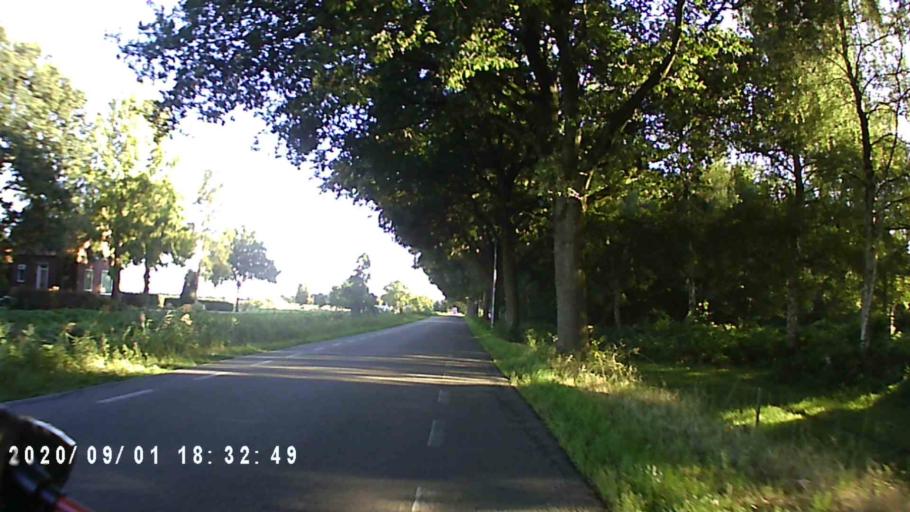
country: NL
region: Groningen
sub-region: Gemeente Hoogezand-Sappemeer
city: Sappemeer
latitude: 53.1516
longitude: 6.7967
